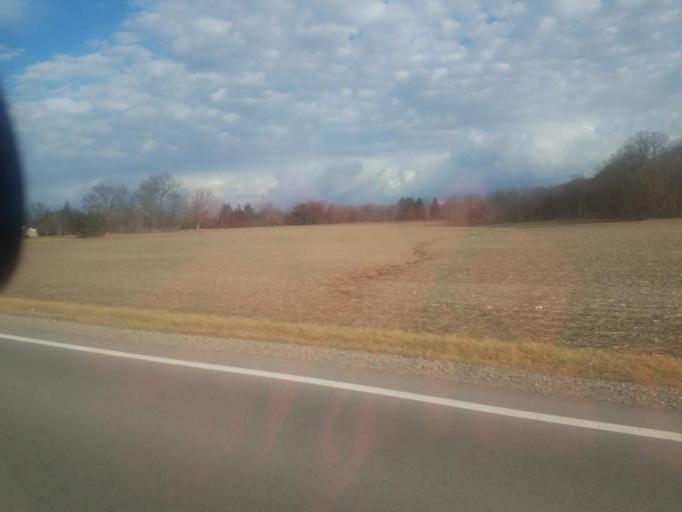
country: US
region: Ohio
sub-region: Marion County
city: Marion
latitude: 40.4983
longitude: -83.0648
